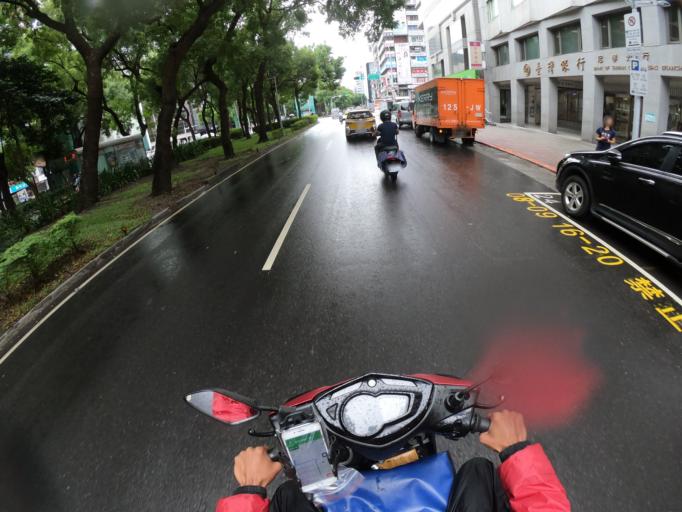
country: TW
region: Taipei
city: Taipei
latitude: 25.0429
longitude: 121.5489
